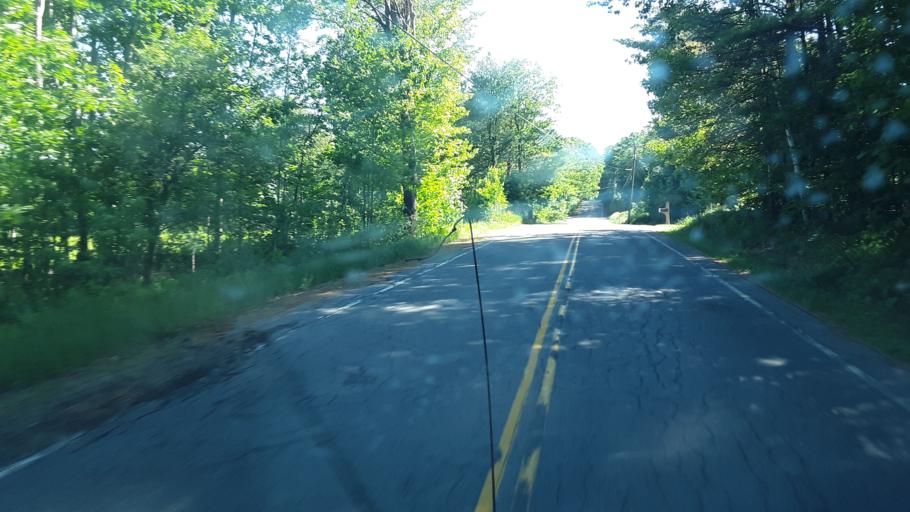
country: US
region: New Hampshire
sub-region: Grafton County
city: North Haverhill
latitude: 44.0953
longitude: -71.9428
